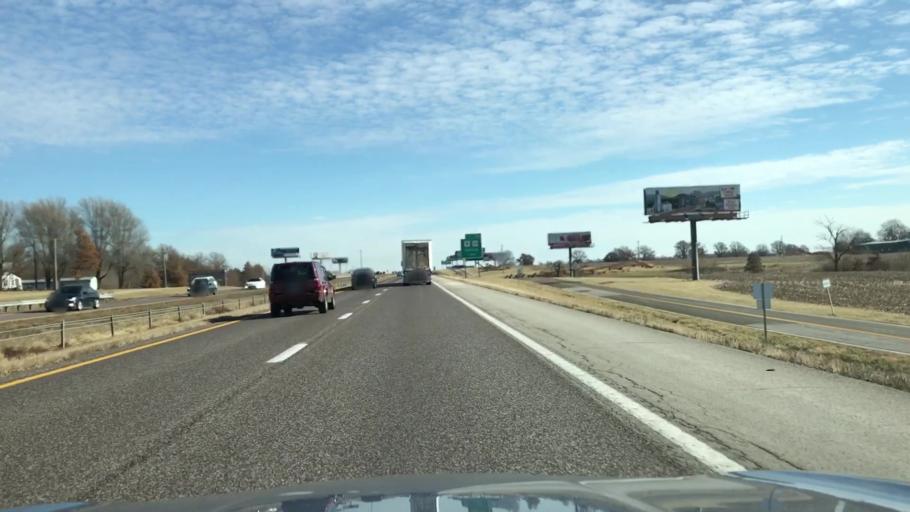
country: US
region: Missouri
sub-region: Callaway County
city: Fulton
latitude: 38.9520
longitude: -92.0322
